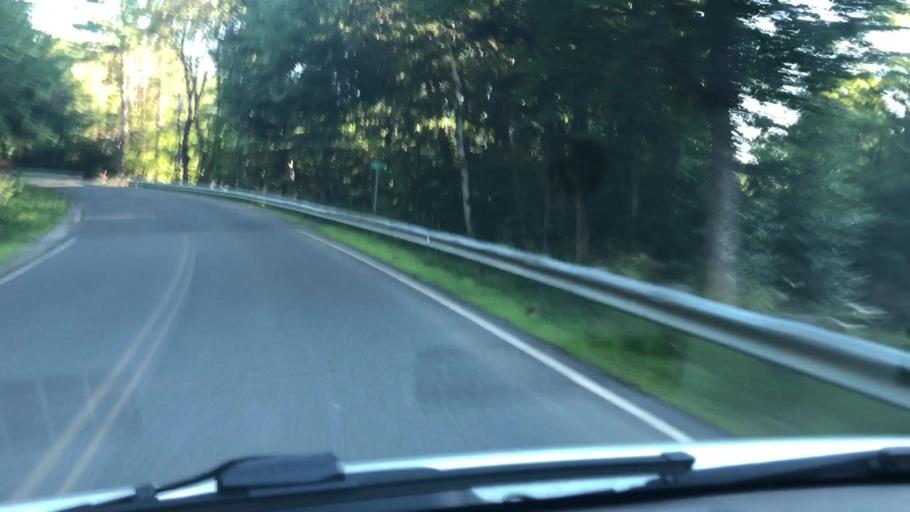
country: US
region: Massachusetts
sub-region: Hampshire County
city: Chesterfield
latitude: 42.4465
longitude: -72.9768
